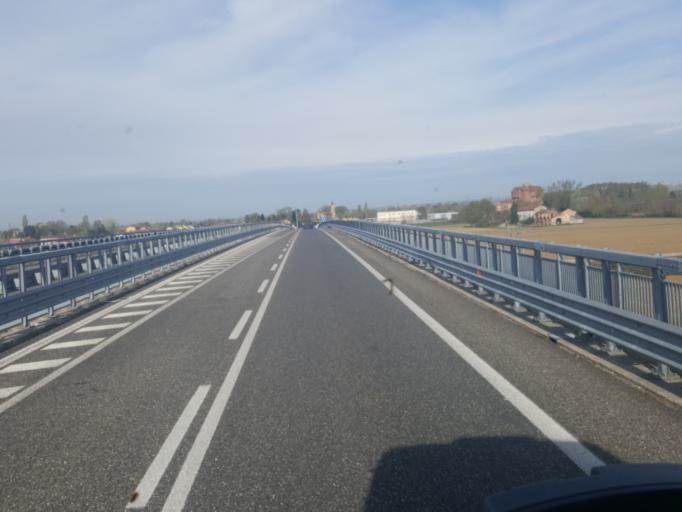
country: IT
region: Piedmont
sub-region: Provincia di Alessandria
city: Alessandria
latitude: 44.9350
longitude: 8.5917
